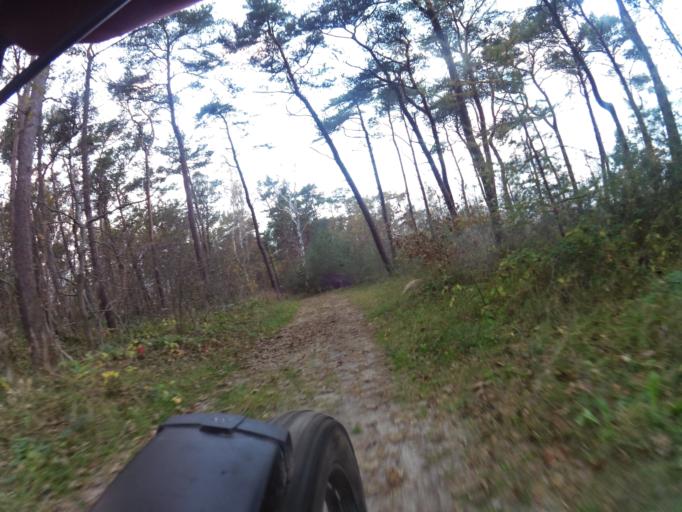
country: PL
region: Pomeranian Voivodeship
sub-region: Powiat pucki
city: Jastarnia
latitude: 54.7284
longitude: 18.6011
